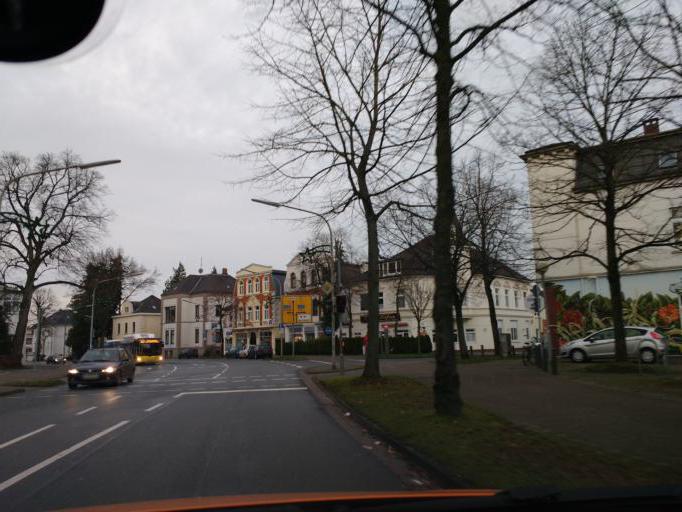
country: DE
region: Lower Saxony
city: Oldenburg
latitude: 53.1305
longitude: 8.2246
